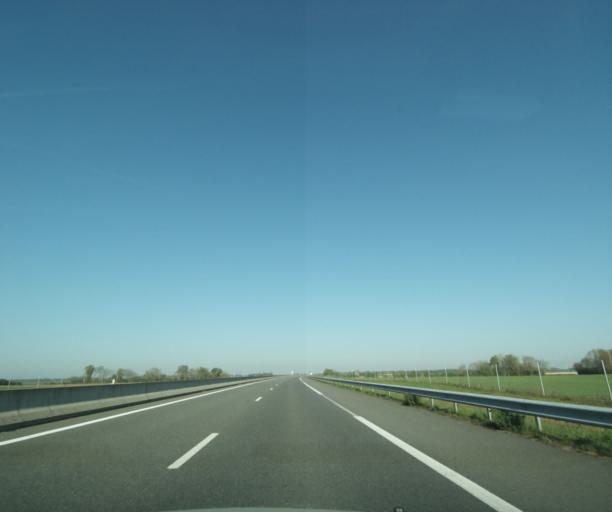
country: FR
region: Centre
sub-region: Departement du Loiret
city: Corbeilles
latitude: 48.0801
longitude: 2.6144
